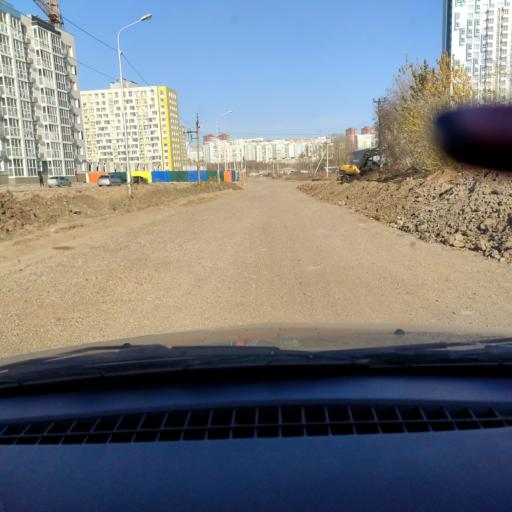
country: RU
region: Bashkortostan
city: Ufa
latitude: 54.6820
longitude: 55.9816
